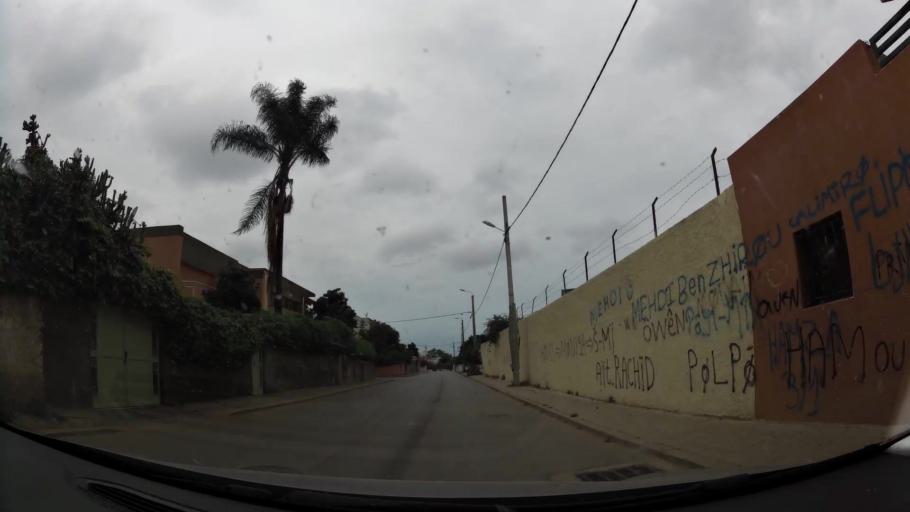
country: MA
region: Rabat-Sale-Zemmour-Zaer
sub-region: Rabat
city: Rabat
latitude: 33.9877
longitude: -6.8212
